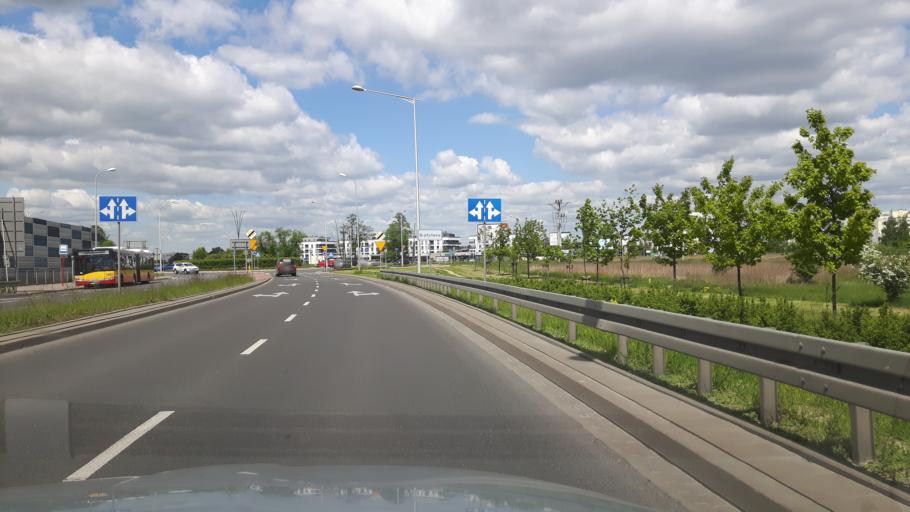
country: PL
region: Masovian Voivodeship
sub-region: Warszawa
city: Targowek
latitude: 52.3089
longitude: 21.0620
